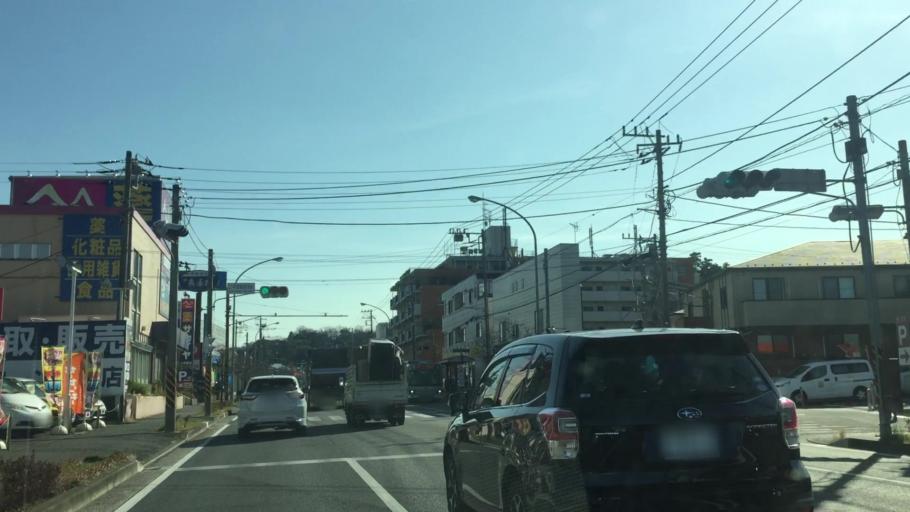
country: JP
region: Kanagawa
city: Yokohama
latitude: 35.3718
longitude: 139.6119
